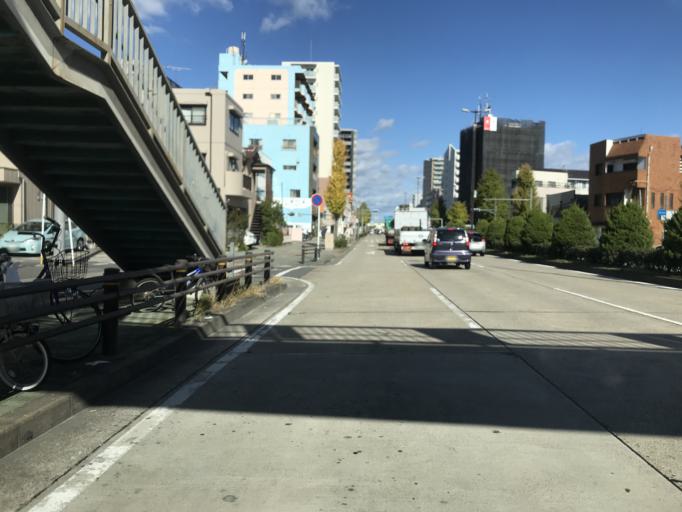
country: JP
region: Aichi
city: Nagoya-shi
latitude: 35.1784
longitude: 136.9397
